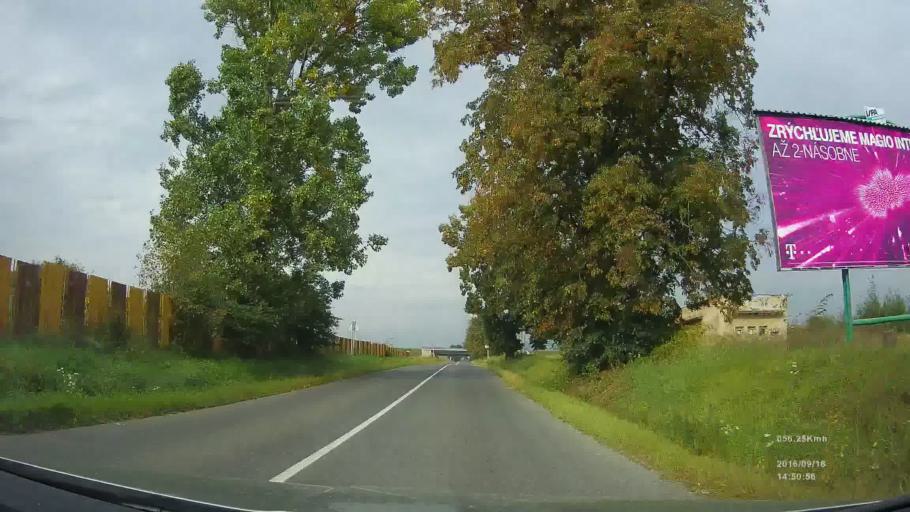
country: SK
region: Presovsky
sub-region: Okres Presov
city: Levoca
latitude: 49.0022
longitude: 20.5838
